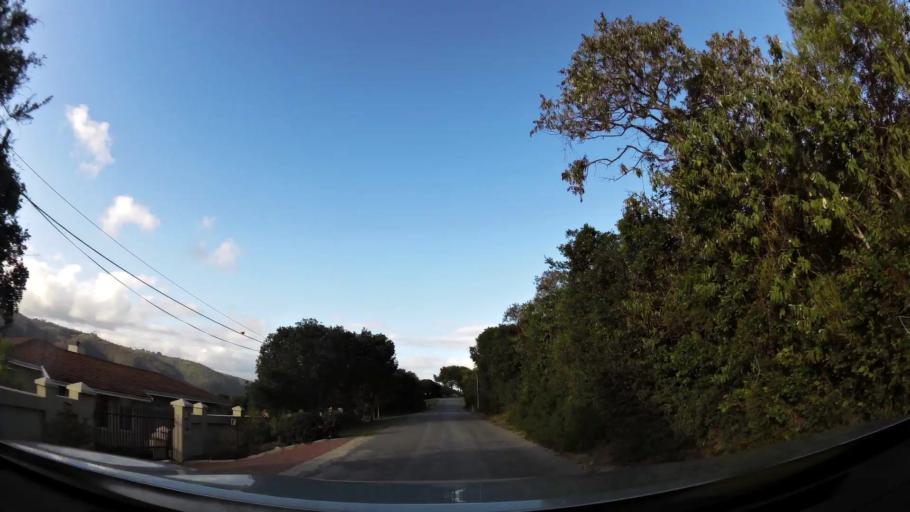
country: ZA
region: Western Cape
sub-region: Eden District Municipality
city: George
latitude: -33.9984
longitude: 22.6229
